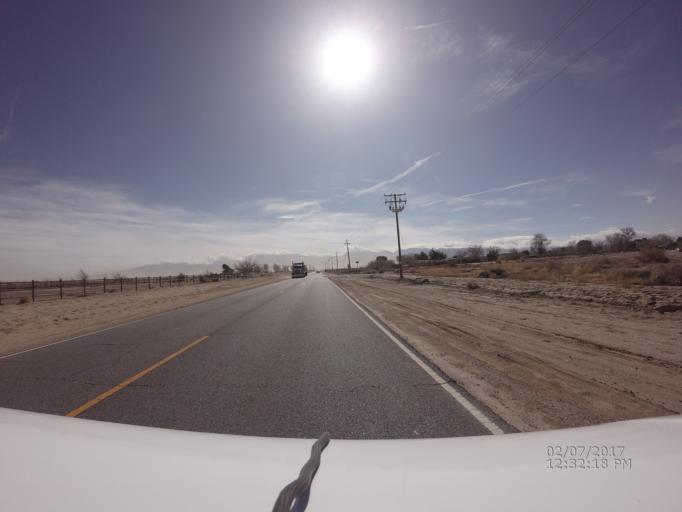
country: US
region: California
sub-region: Los Angeles County
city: Lake Los Angeles
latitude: 34.5952
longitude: -117.8268
